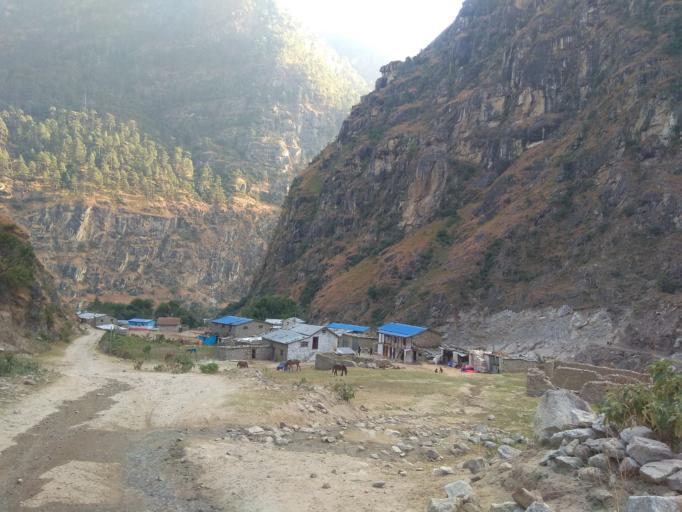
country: NP
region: Far Western
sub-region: Seti Zone
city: Achham
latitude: 29.2213
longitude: 81.6311
